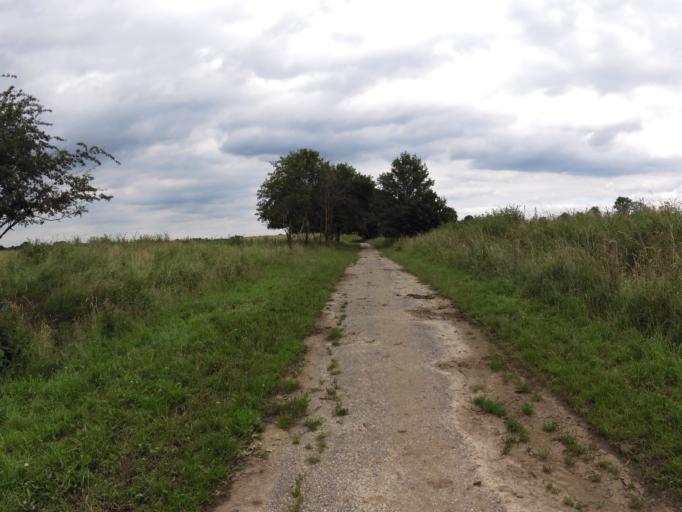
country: NL
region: North Brabant
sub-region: Gemeente Landerd
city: Reek
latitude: 51.7688
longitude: 5.6843
